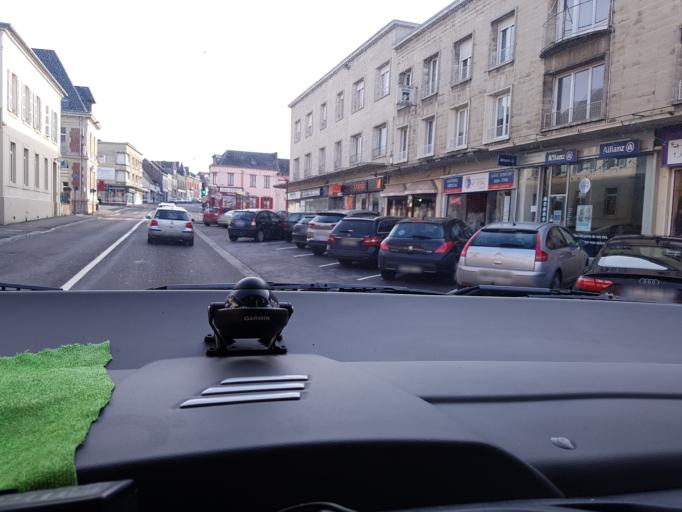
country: FR
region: Picardie
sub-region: Departement de l'Aisne
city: Hirson
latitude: 49.9235
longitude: 4.0816
